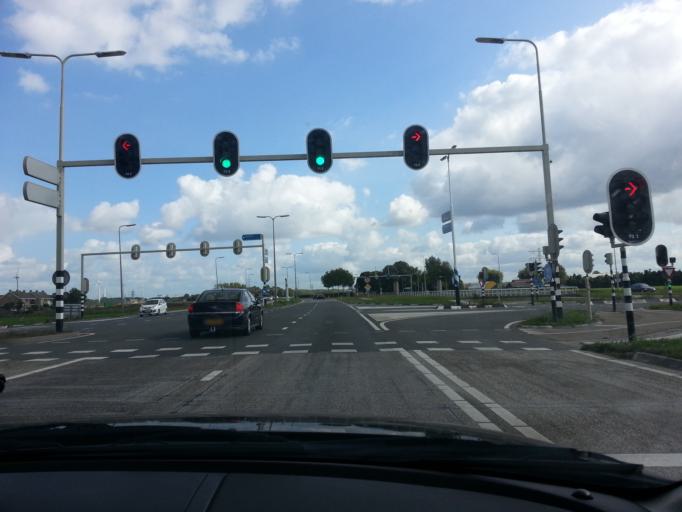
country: NL
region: South Holland
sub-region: Gemeente Maassluis
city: Maassluis
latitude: 51.8588
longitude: 4.2616
